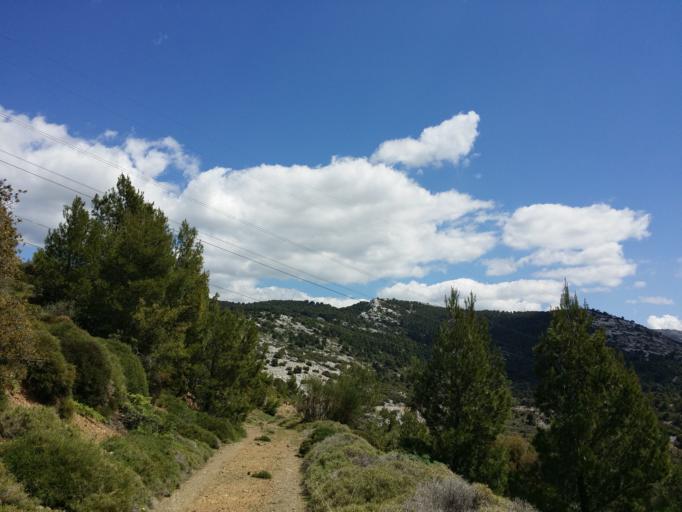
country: GR
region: Attica
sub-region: Nomarchia Dytikis Attikis
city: Fyli
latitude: 38.1412
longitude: 23.6390
